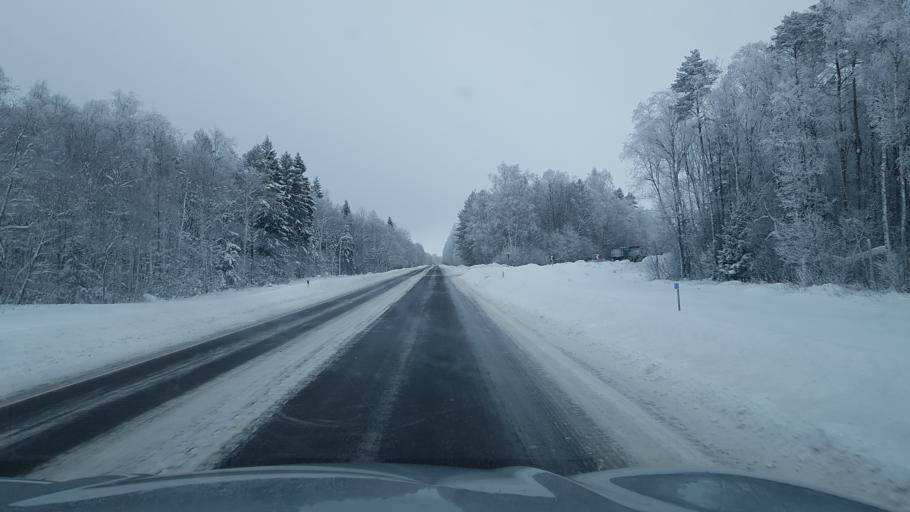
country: EE
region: Ida-Virumaa
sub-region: Johvi vald
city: Johvi
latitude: 59.2951
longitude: 27.3983
